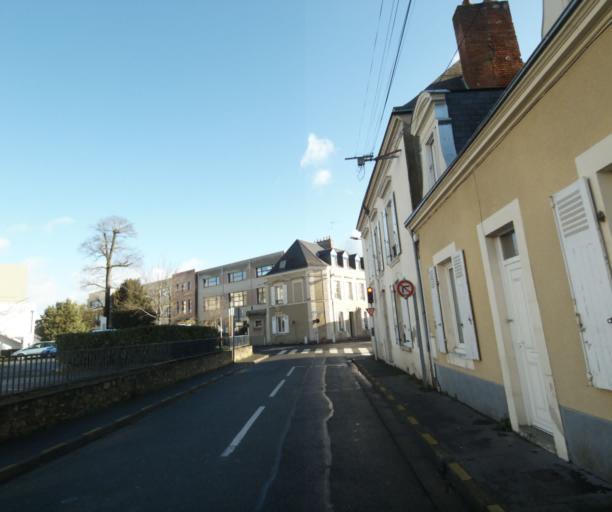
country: FR
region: Pays de la Loire
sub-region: Departement de la Sarthe
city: Le Mans
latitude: 48.0056
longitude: 0.1845
